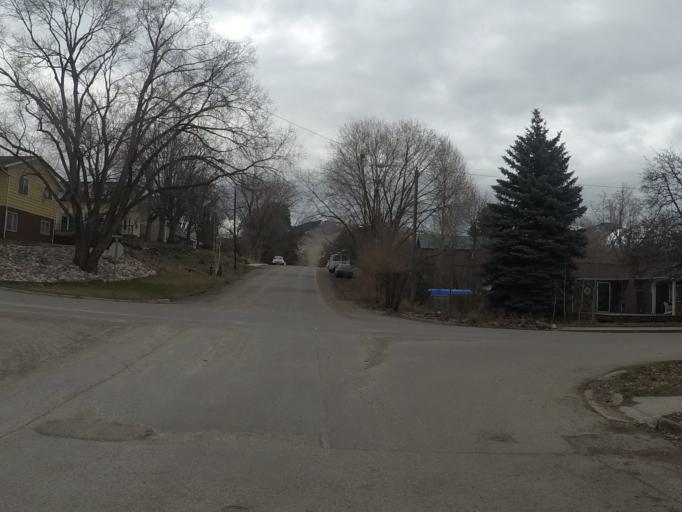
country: US
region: Montana
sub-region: Missoula County
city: Missoula
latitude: 46.8790
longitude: -114.0111
